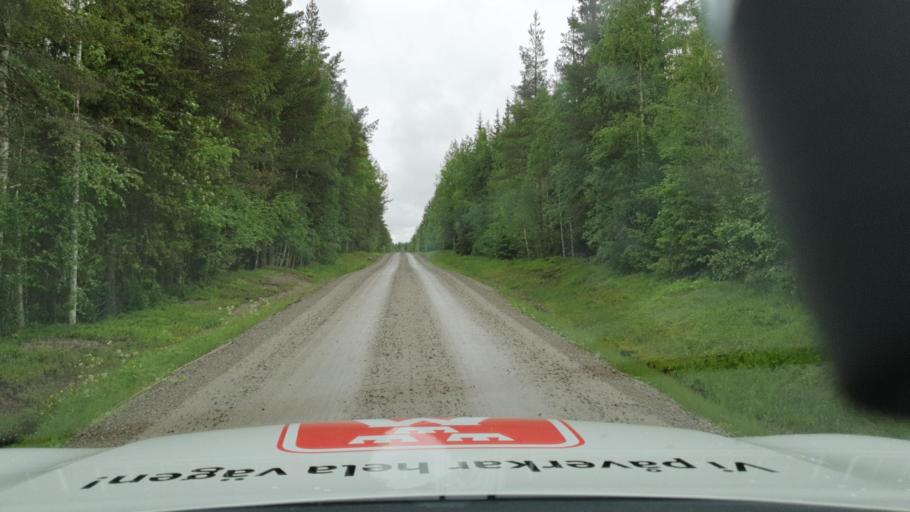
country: SE
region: Vaesterbotten
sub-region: Dorotea Kommun
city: Dorotea
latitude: 64.0040
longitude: 16.7988
